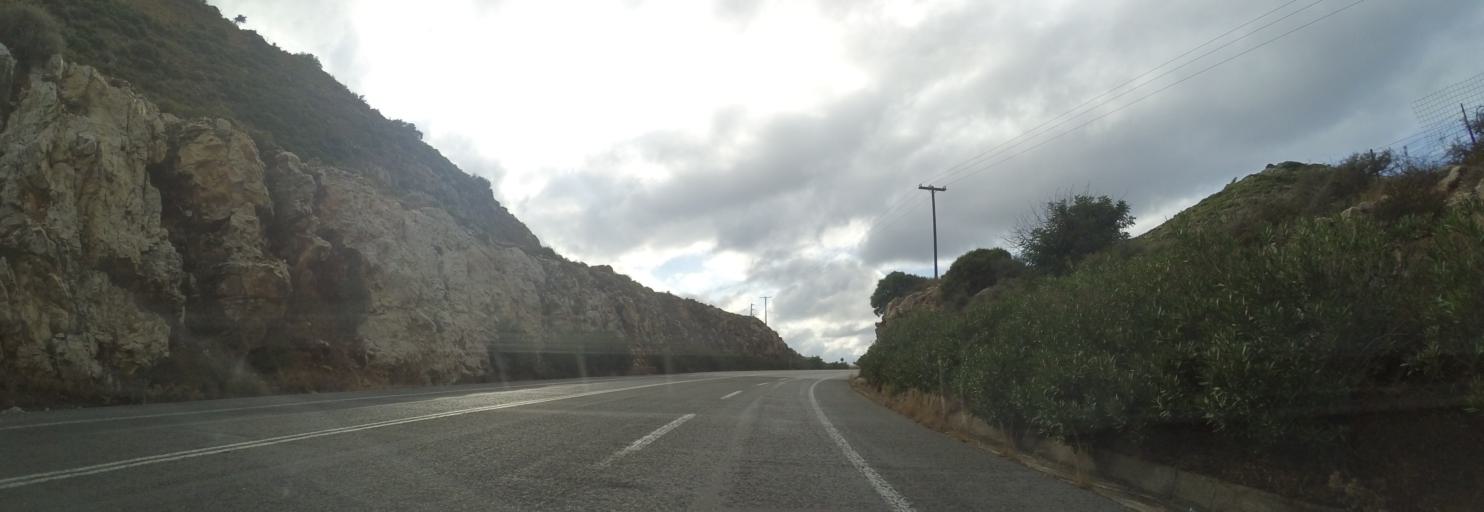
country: GR
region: Crete
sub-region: Nomos Rethymnis
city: Perama
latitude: 35.4067
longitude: 24.7586
